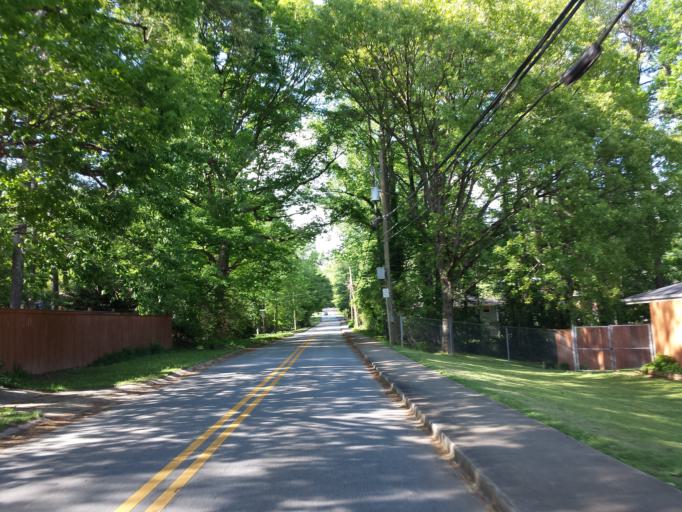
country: US
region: Georgia
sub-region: Cobb County
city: Smyrna
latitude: 33.8696
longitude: -84.5231
